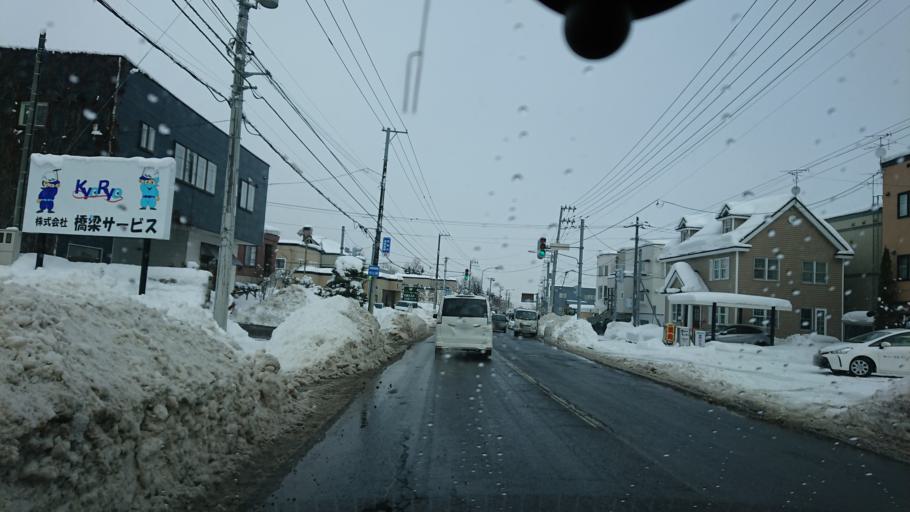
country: JP
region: Hokkaido
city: Sapporo
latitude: 42.9685
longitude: 141.3429
